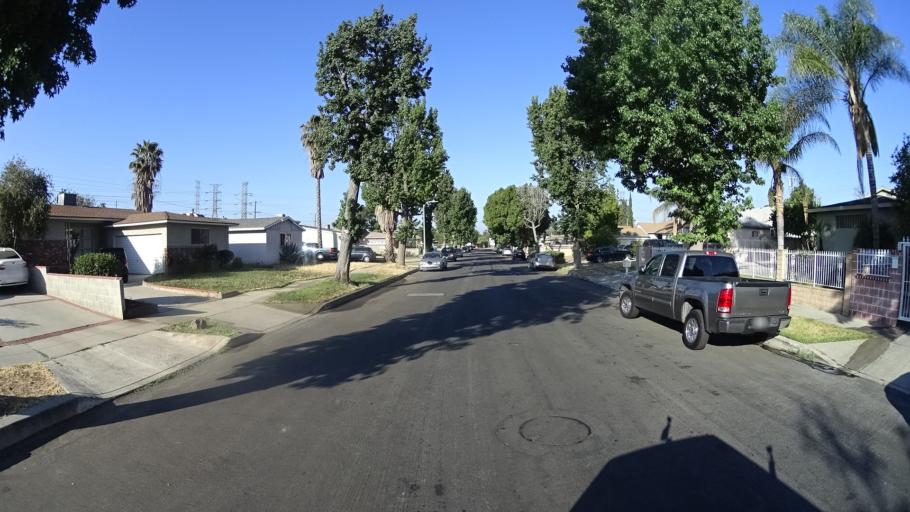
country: US
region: California
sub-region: Los Angeles County
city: Van Nuys
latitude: 34.2279
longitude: -118.4185
